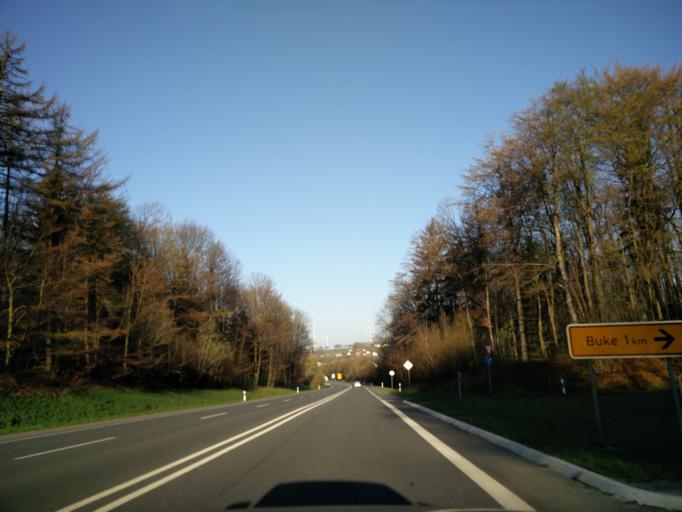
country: DE
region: North Rhine-Westphalia
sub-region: Regierungsbezirk Detmold
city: Altenbeken
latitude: 51.7399
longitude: 8.9616
